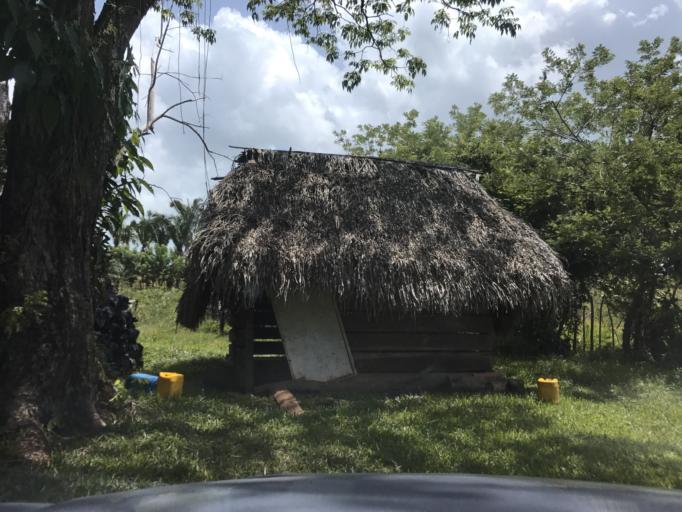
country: GT
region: Izabal
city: Morales
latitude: 15.6205
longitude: -89.0507
